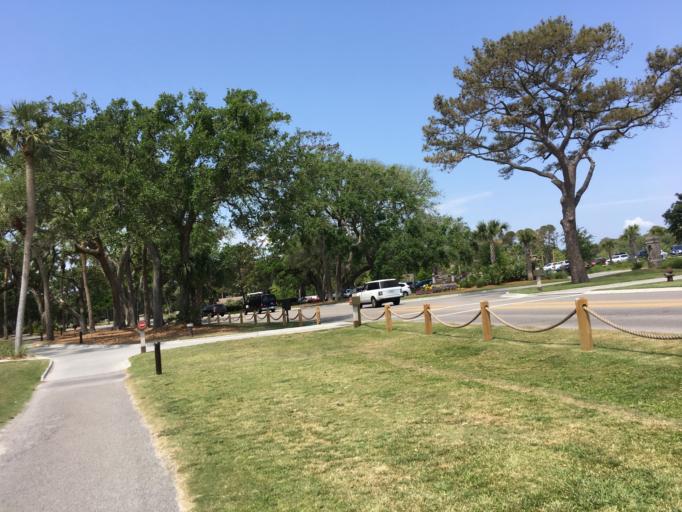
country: US
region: South Carolina
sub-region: Beaufort County
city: Hilton Head Island
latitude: 32.1266
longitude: -80.7898
